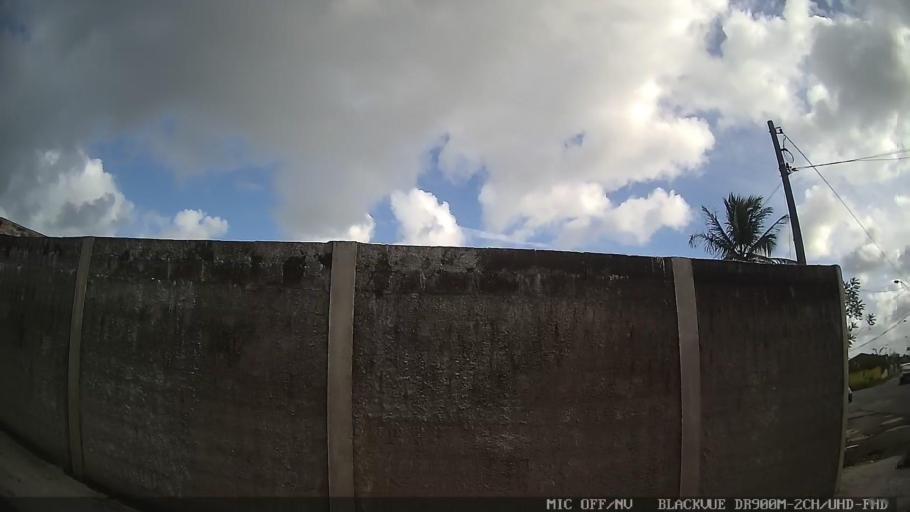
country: BR
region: Sao Paulo
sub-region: Itanhaem
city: Itanhaem
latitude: -24.1918
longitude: -46.8142
